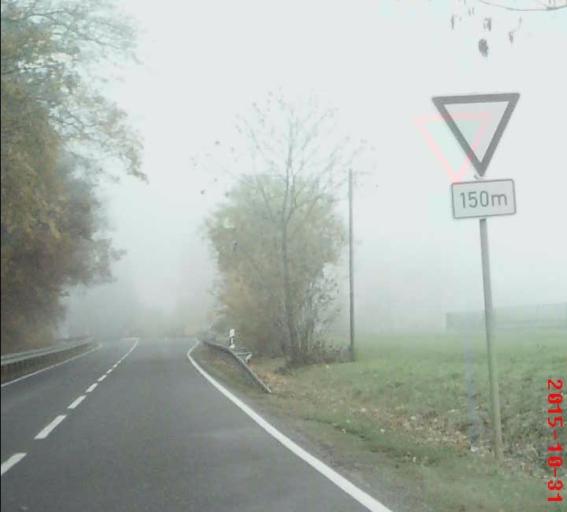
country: DE
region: Thuringia
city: Buttstedt
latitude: 51.2124
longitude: 10.3182
